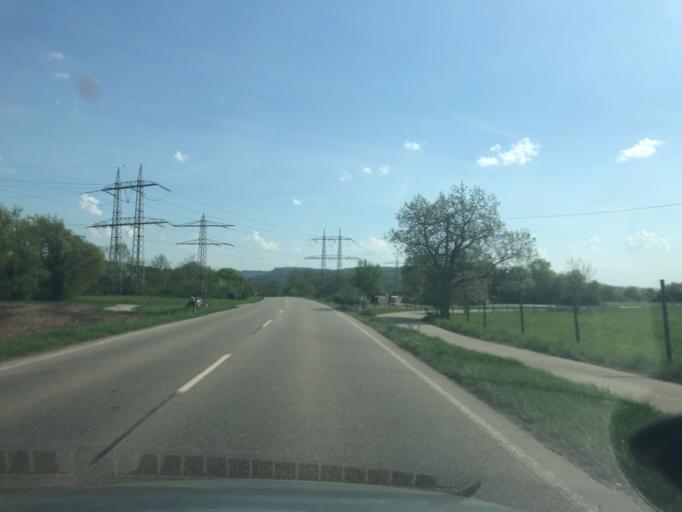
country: CH
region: Aargau
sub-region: Bezirk Zurzach
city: Koblenz
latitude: 47.6313
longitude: 8.2526
